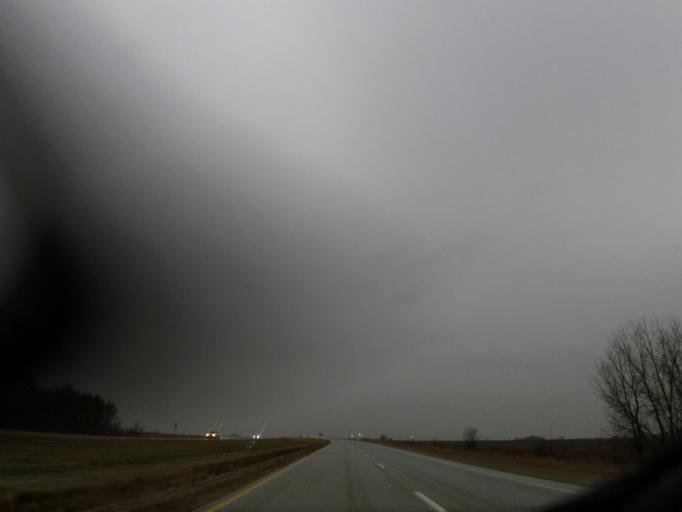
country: US
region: Iowa
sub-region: Cerro Gordo County
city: Mason City
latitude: 43.1119
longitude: -93.1609
